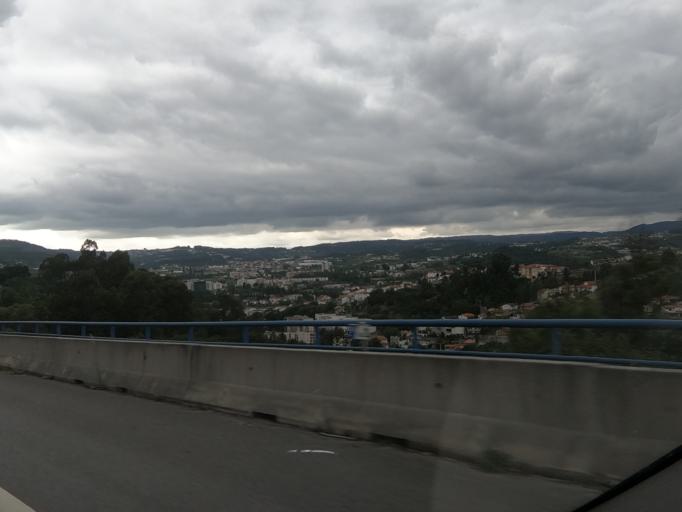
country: PT
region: Porto
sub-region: Amarante
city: Amarante
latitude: 41.2606
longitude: -8.0642
